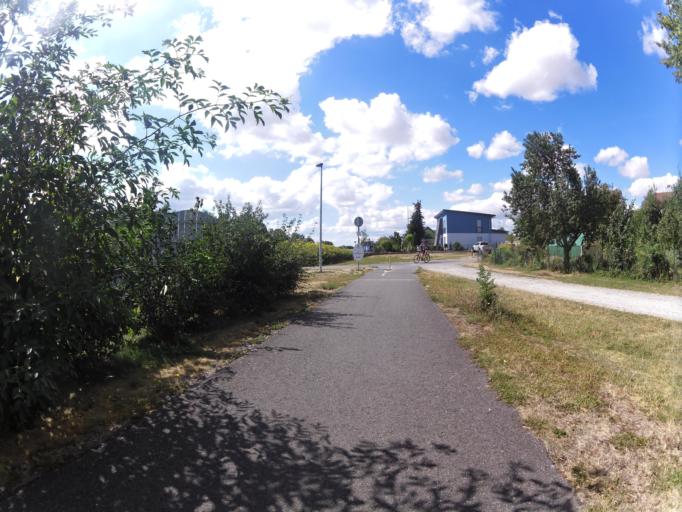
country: DE
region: Bavaria
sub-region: Regierungsbezirk Unterfranken
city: Sonderhofen
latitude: 49.5705
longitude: 10.0195
